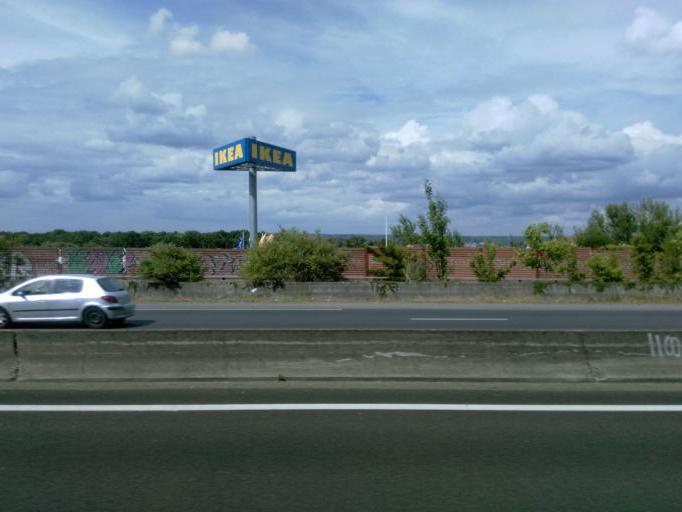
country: FR
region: Ile-de-France
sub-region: Departement du Val-d'Oise
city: Montigny-les-Cormeilles
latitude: 48.9863
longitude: 2.2112
